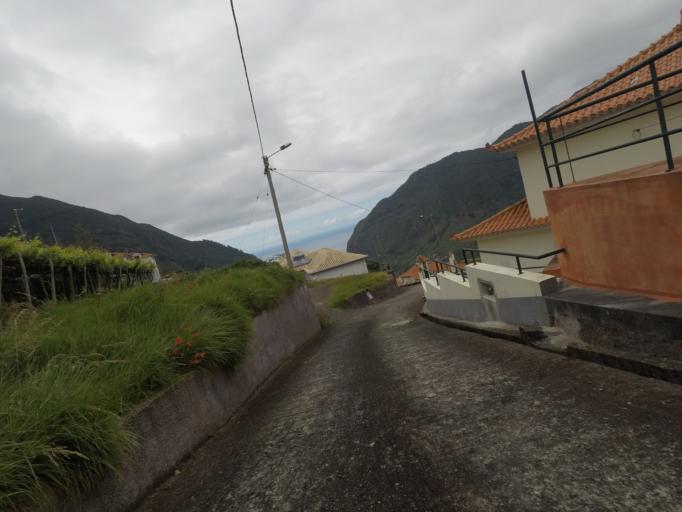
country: PT
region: Madeira
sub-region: Sao Vicente
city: Sao Vicente
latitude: 32.7826
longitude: -17.0426
